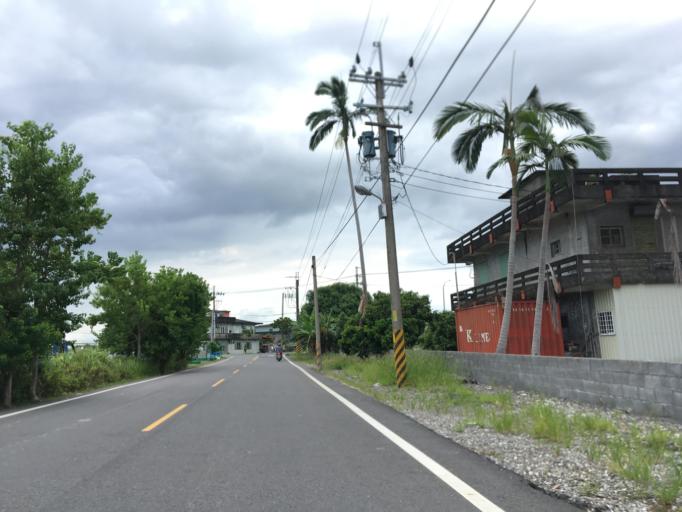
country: TW
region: Taiwan
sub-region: Yilan
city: Yilan
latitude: 24.6880
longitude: 121.8044
